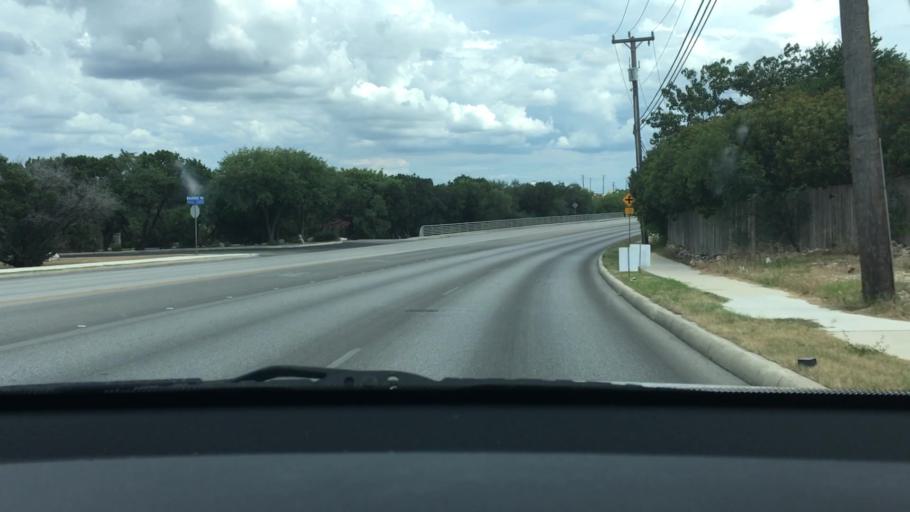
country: US
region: Texas
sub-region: Bexar County
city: Timberwood Park
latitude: 29.6517
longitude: -98.4262
